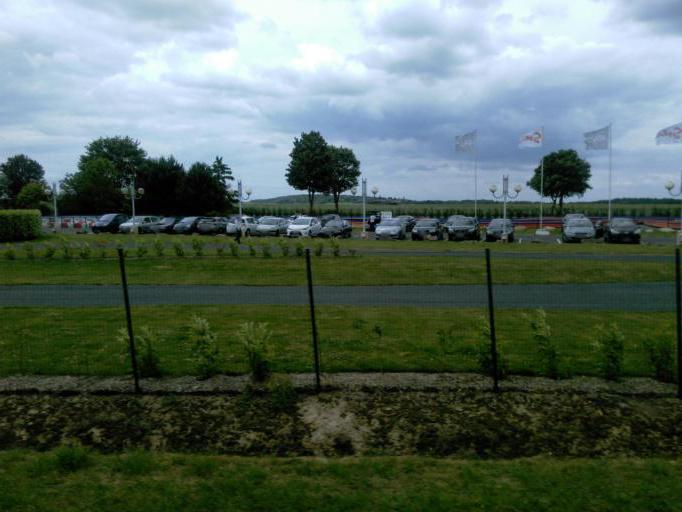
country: FR
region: Ile-de-France
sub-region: Departement du Val-d'Oise
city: Osny
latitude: 49.1019
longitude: 2.0397
